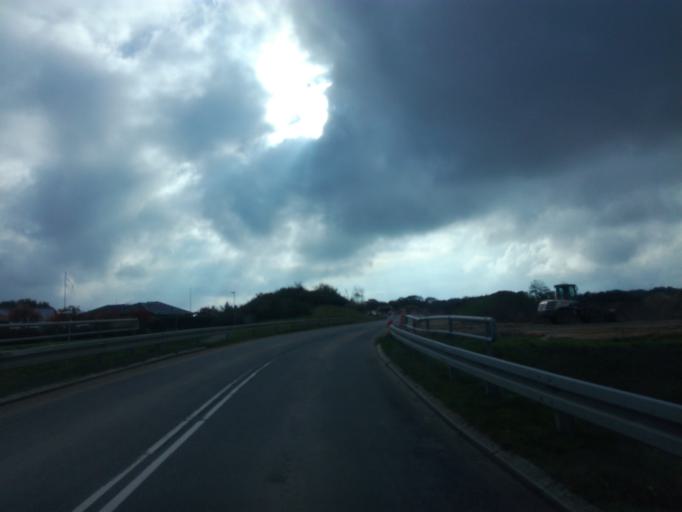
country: DK
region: South Denmark
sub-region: Vejle Kommune
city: Borkop
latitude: 55.6372
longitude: 9.6408
